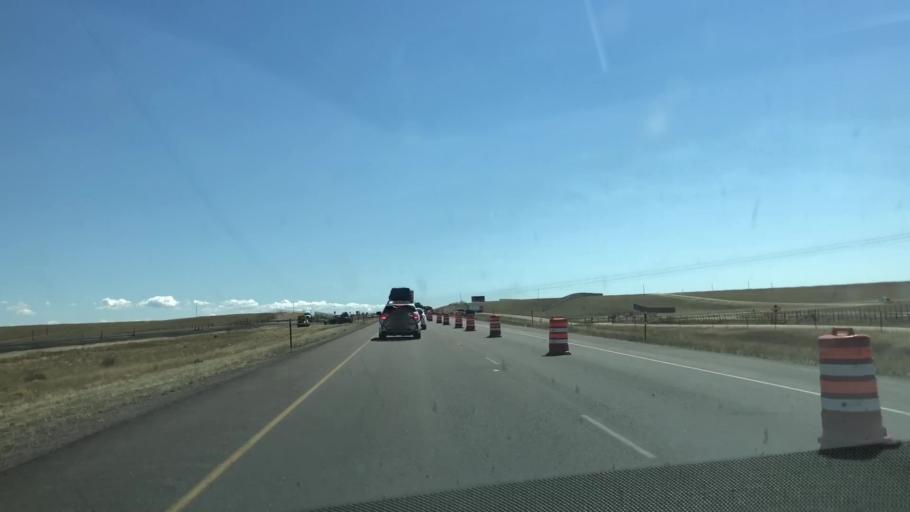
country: US
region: Wyoming
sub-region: Albany County
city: Laramie
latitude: 41.5449
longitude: -106.0857
